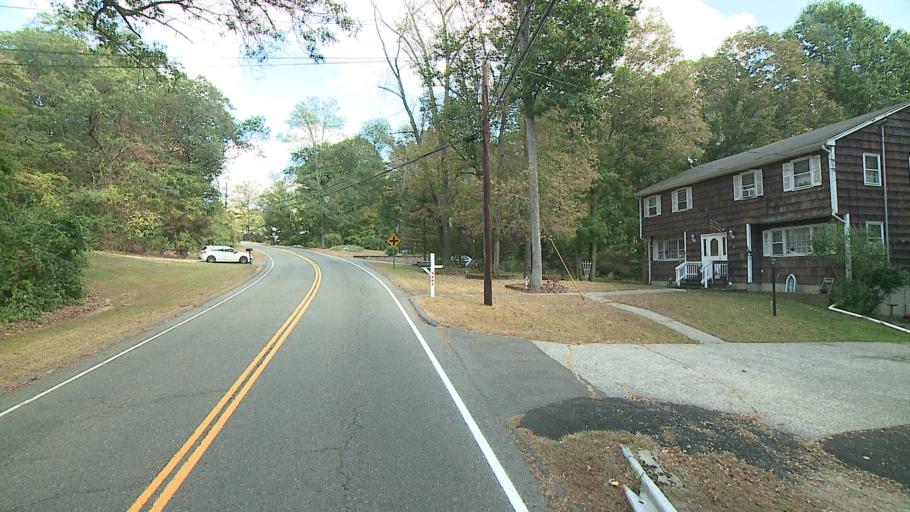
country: US
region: Connecticut
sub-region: New Haven County
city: Naugatuck
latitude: 41.4463
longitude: -73.0352
